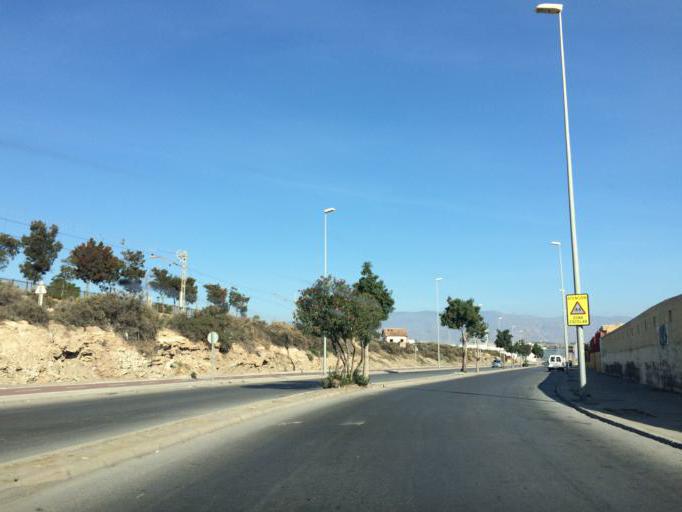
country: ES
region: Andalusia
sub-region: Provincia de Almeria
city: Almeria
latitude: 36.8489
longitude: -2.4337
